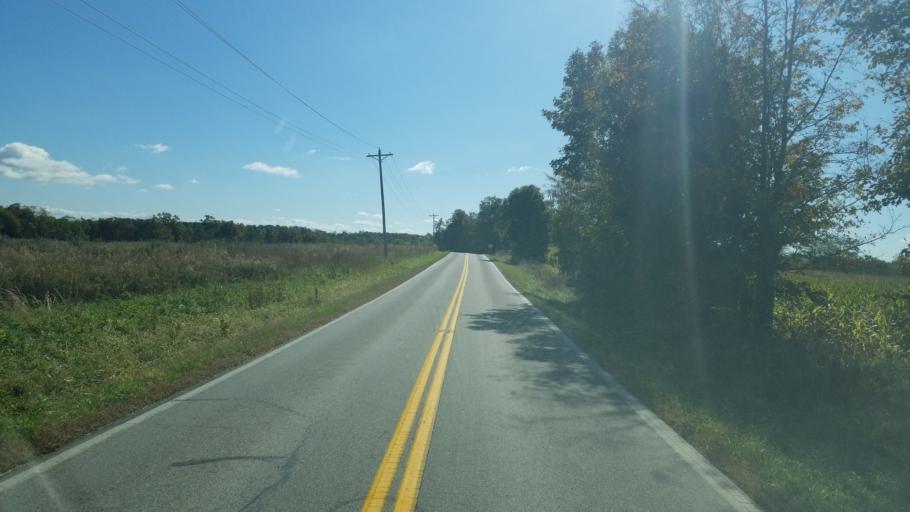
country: US
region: Ohio
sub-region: Highland County
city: Leesburg
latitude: 39.2773
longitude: -83.4890
